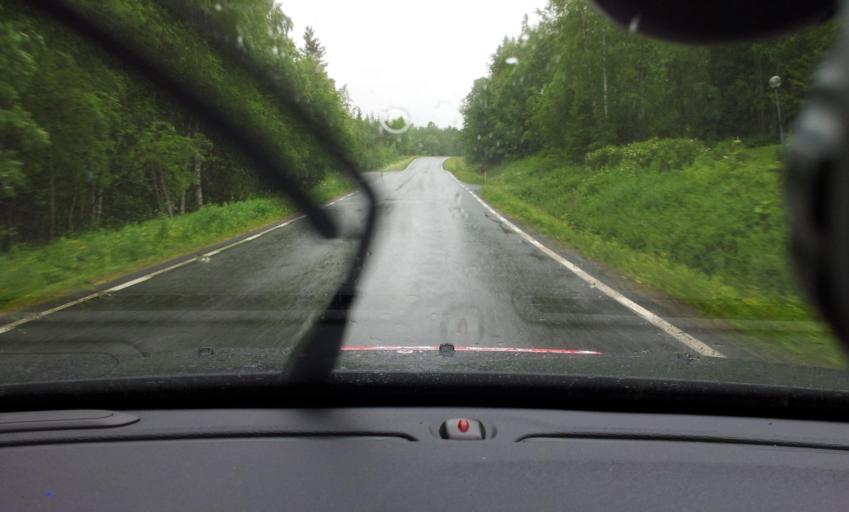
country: SE
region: Jaemtland
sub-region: Are Kommun
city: Are
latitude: 63.3142
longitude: 13.1564
